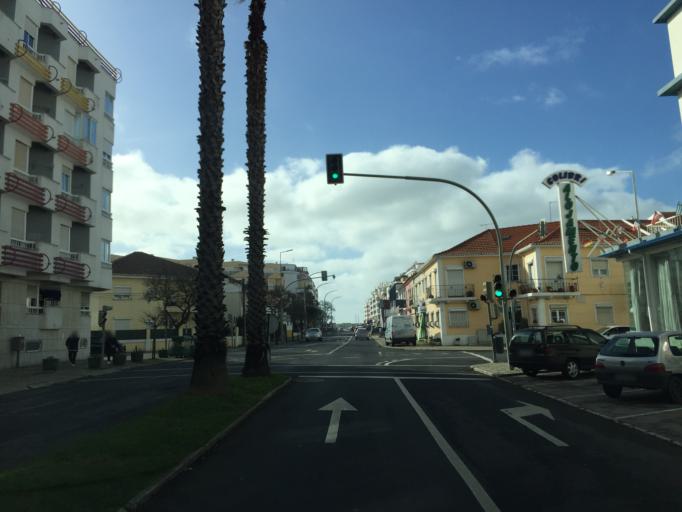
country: PT
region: Setubal
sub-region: Almada
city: Costa de Caparica
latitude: 38.6457
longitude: -9.2352
